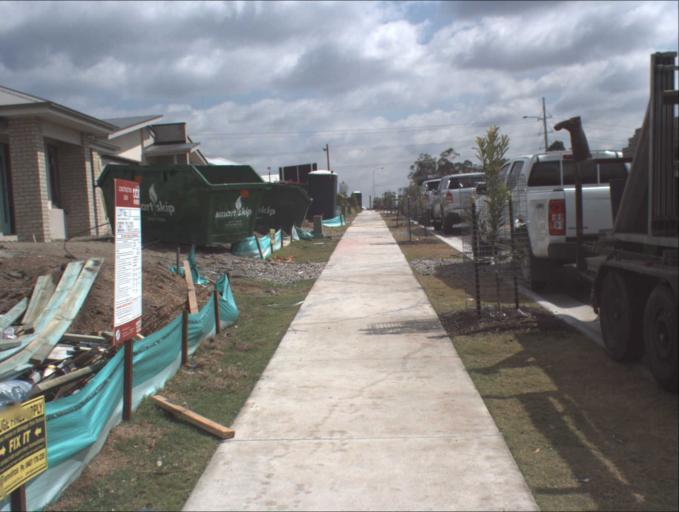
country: AU
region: Queensland
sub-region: Logan
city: Woodridge
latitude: -27.6635
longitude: 153.0832
